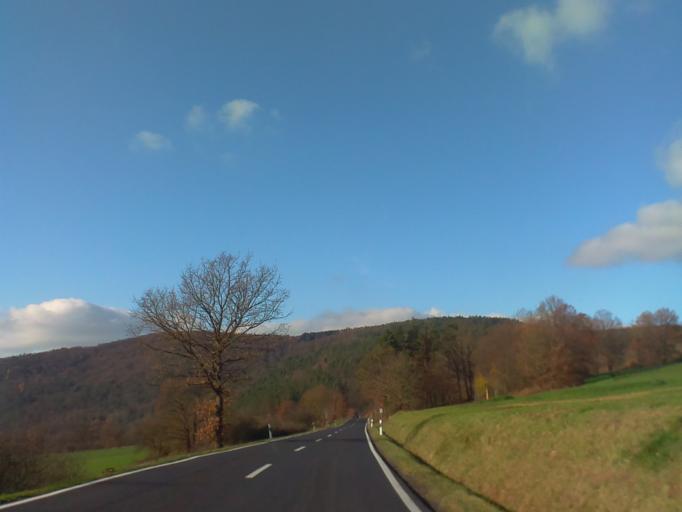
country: DE
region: Bavaria
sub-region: Regierungsbezirk Unterfranken
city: Bad Bocklet
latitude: 50.2977
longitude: 10.1206
